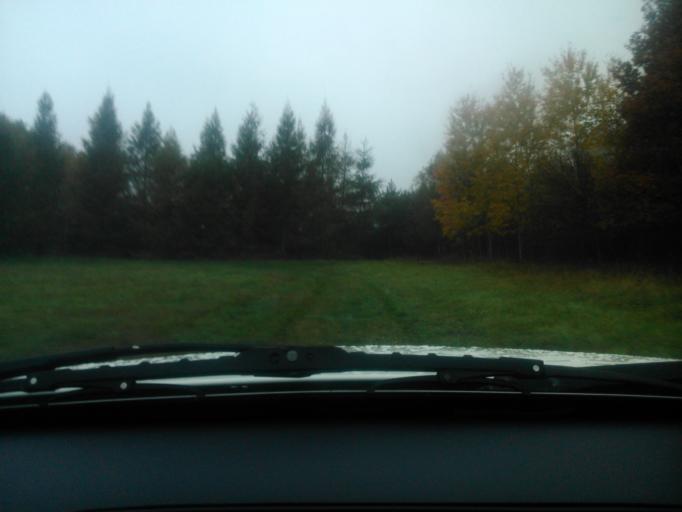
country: PL
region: Kujawsko-Pomorskie
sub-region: Powiat golubsko-dobrzynski
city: Radomin
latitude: 53.1524
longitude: 19.1351
